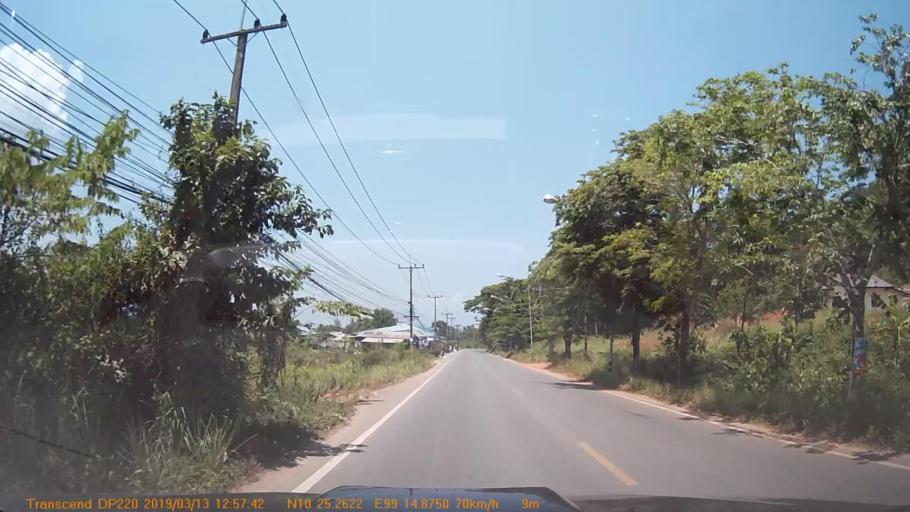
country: TH
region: Chumphon
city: Chumphon
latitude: 10.4215
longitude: 99.2478
